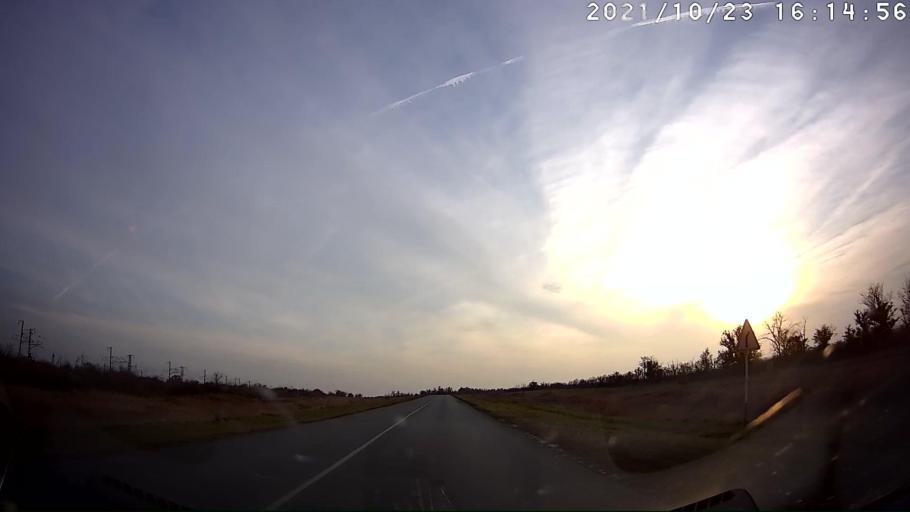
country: RU
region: Volgograd
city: Kotel'nikovo
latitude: 47.9399
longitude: 43.6013
